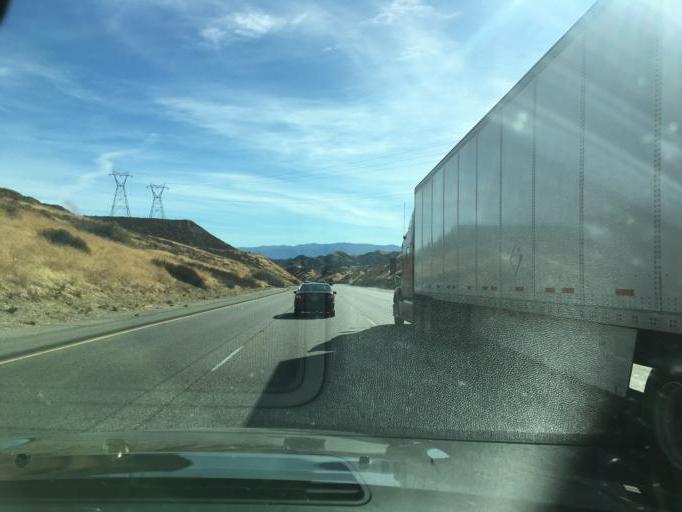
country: US
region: California
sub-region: Los Angeles County
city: Castaic
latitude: 34.5316
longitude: -118.6443
